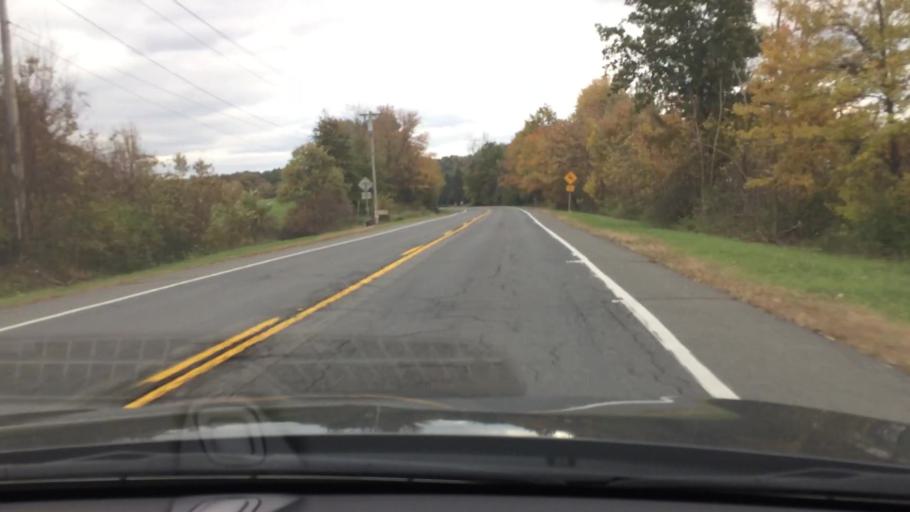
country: US
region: New York
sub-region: Columbia County
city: Oakdale
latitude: 42.1497
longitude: -73.7458
